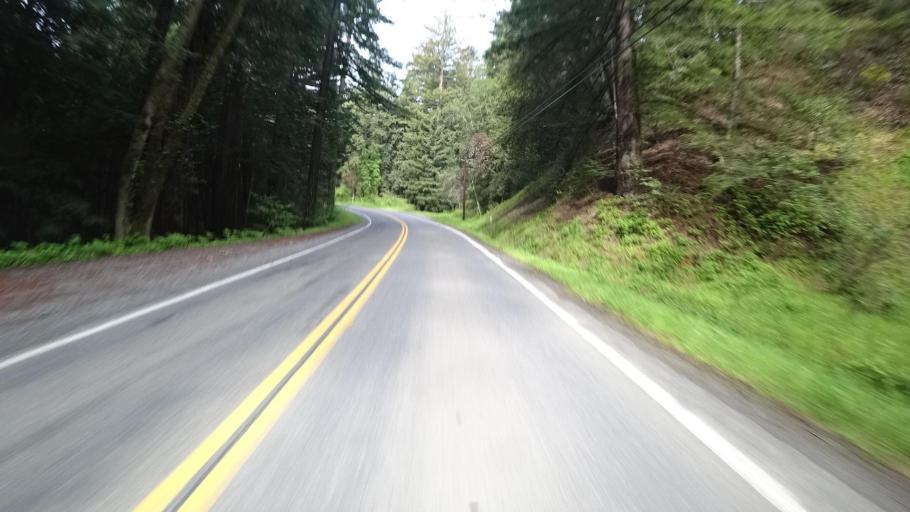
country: US
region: California
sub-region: Humboldt County
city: Redway
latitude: 40.2238
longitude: -123.8025
